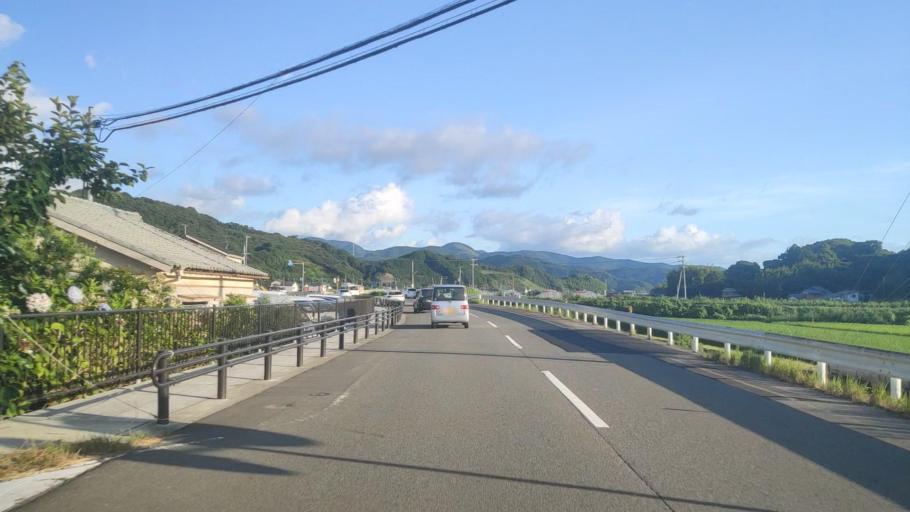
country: JP
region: Wakayama
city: Tanabe
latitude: 33.7189
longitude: 135.4459
